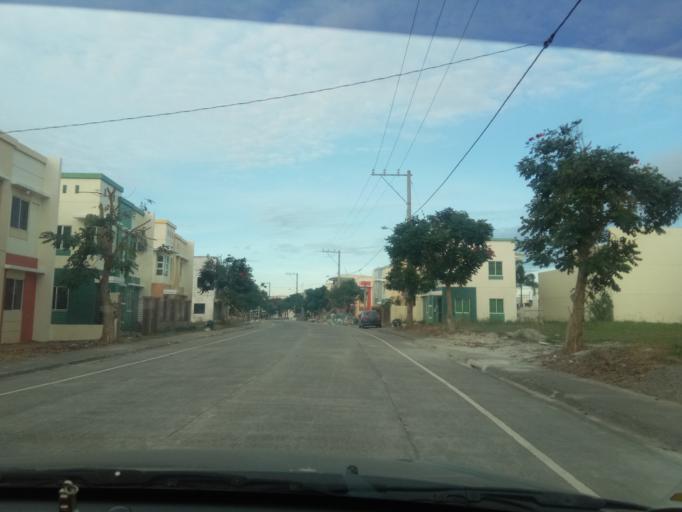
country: PH
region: Calabarzon
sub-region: Province of Cavite
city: Biga
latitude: 14.2758
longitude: 120.9680
